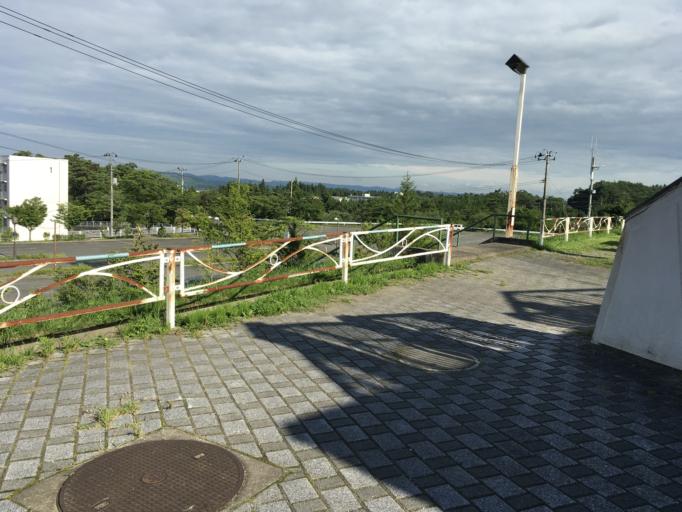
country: JP
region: Iwate
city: Ichinoseki
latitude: 38.8350
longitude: 141.1702
